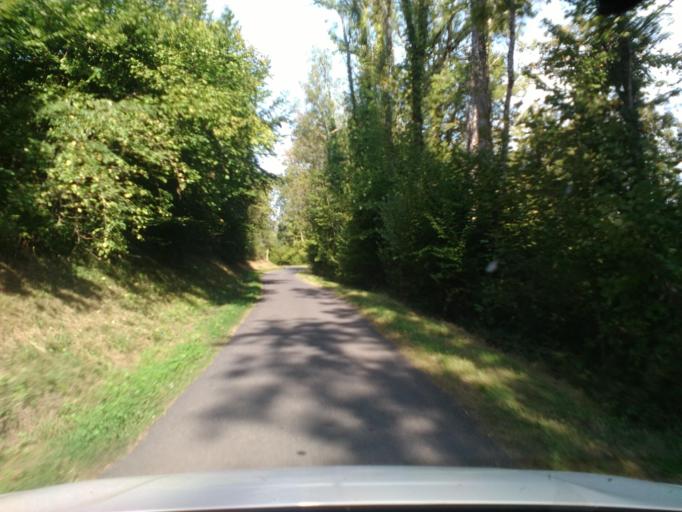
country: FR
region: Lorraine
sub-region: Departement des Vosges
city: Senones
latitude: 48.3546
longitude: 7.0060
